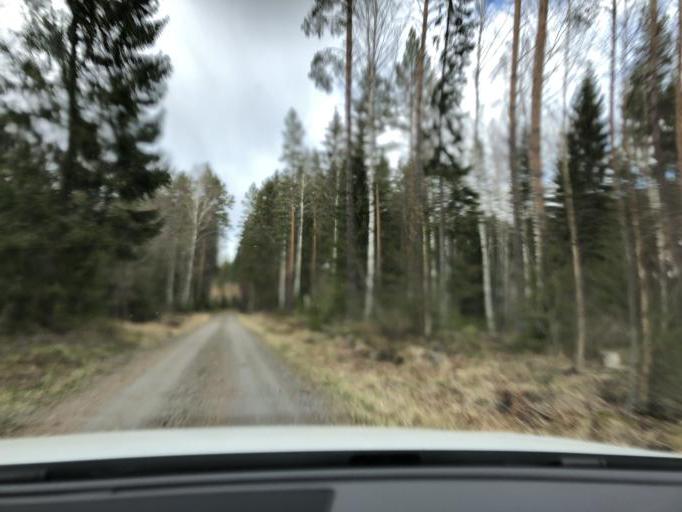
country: SE
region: Gaevleborg
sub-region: Gavle Kommun
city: Hedesunda
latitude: 60.3258
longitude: 17.1054
